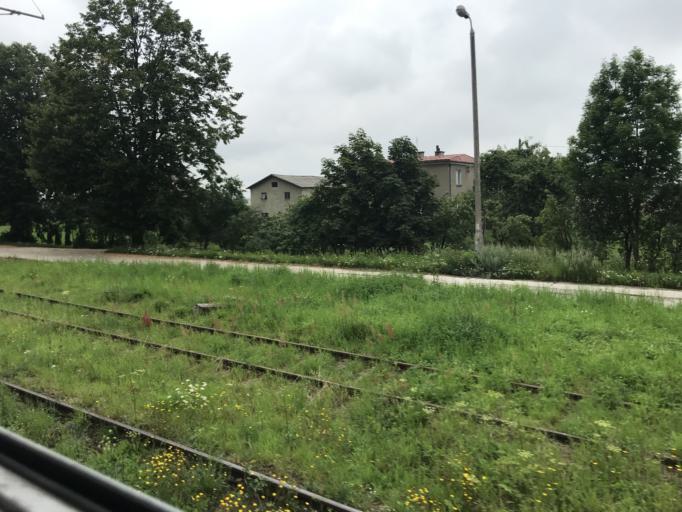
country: PL
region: Warmian-Masurian Voivodeship
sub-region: Powiat elblaski
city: Gronowo Elblaskie
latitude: 54.0916
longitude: 19.3100
